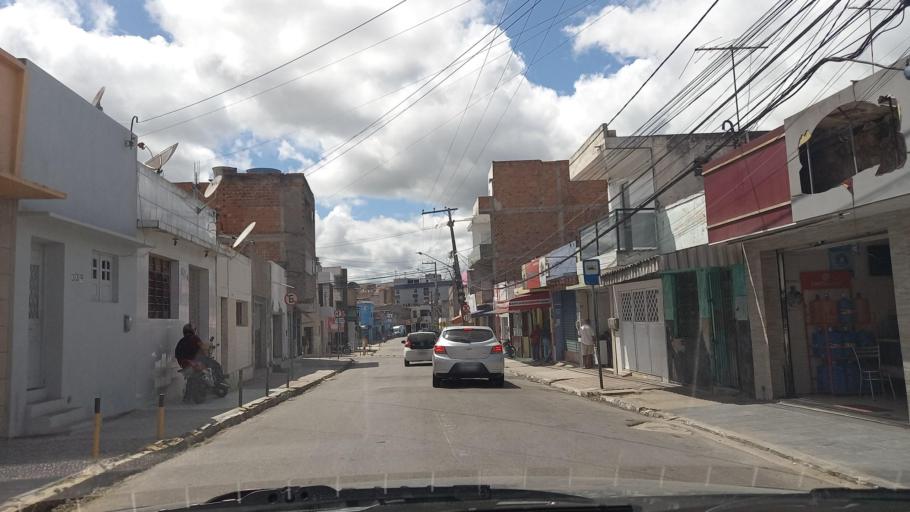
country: BR
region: Pernambuco
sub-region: Caruaru
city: Caruaru
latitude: -8.2837
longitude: -35.9640
